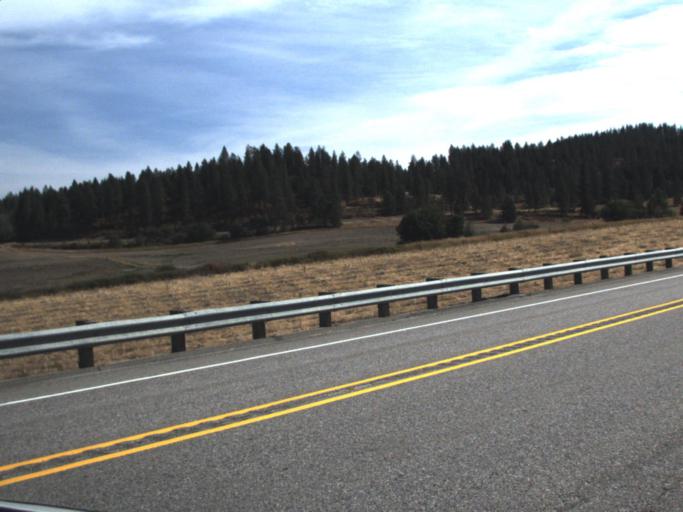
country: US
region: Washington
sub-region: Stevens County
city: Chewelah
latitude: 48.1971
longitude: -117.7070
